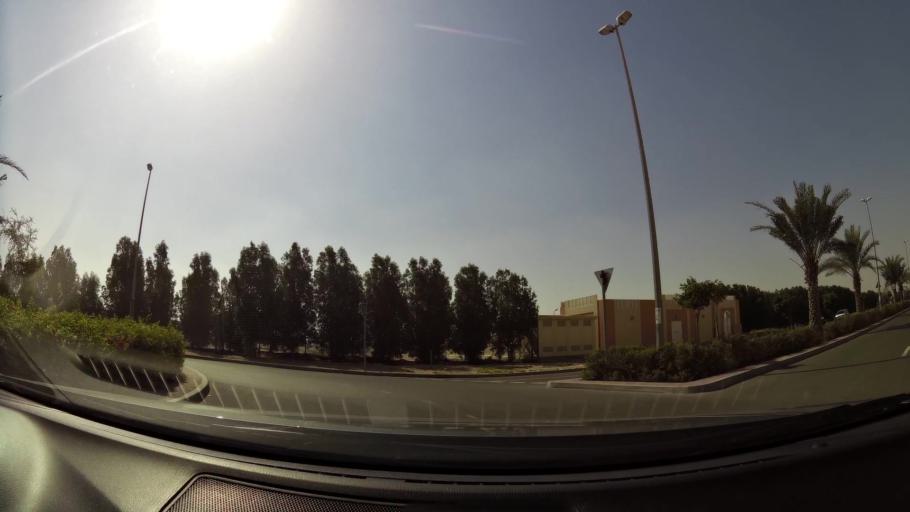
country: AE
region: Dubai
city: Dubai
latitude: 24.9507
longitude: 55.0511
